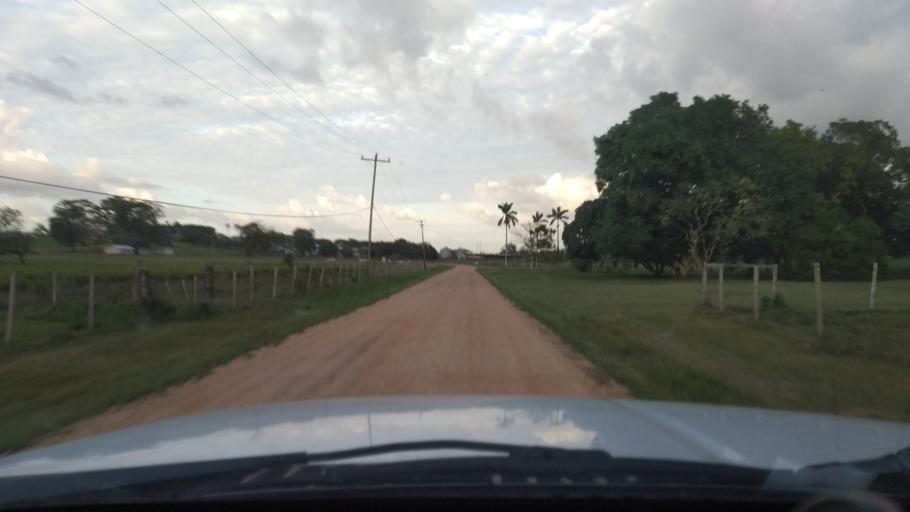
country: BZ
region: Cayo
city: San Ignacio
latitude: 17.2241
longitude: -88.9950
